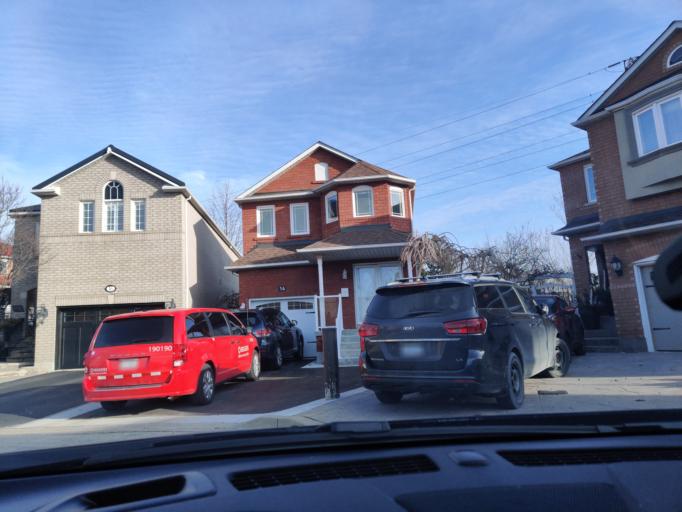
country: CA
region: Ontario
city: Toronto
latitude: 43.7000
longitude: -79.4500
